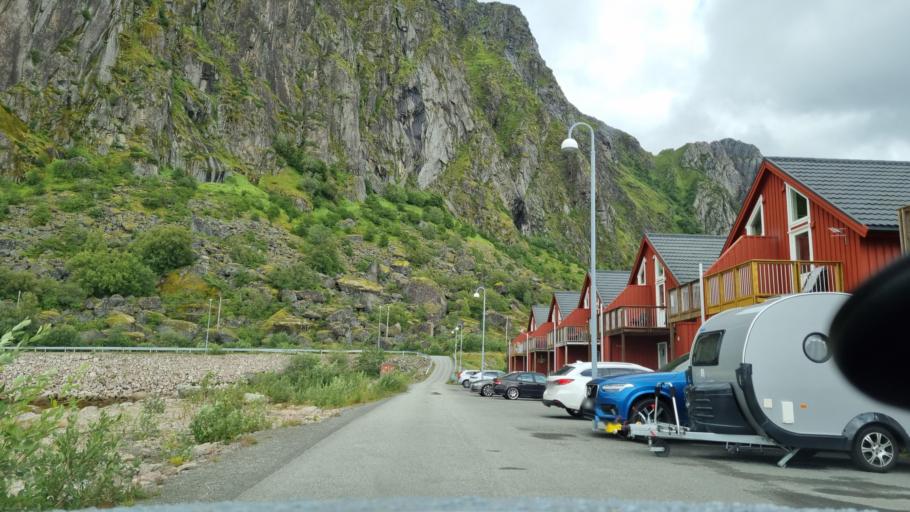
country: NO
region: Nordland
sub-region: Vagan
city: Svolvaer
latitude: 68.2409
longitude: 14.5907
